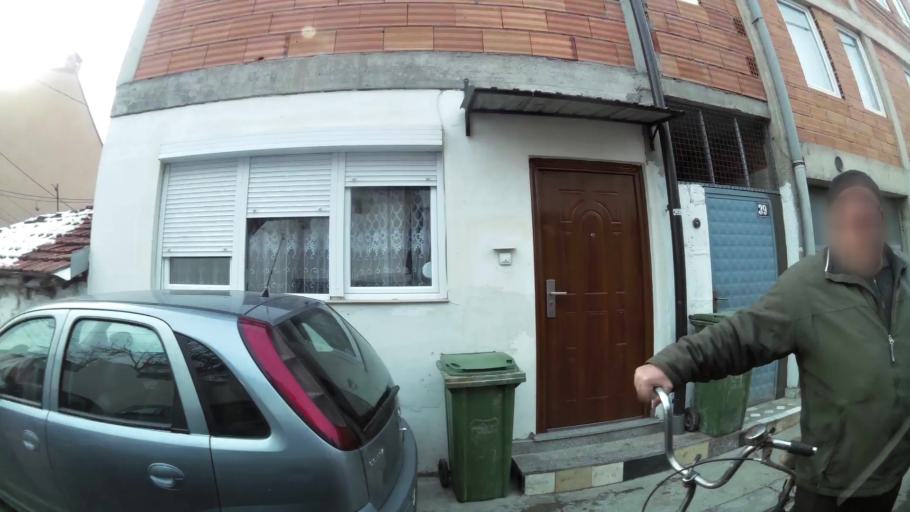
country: MK
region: Cair
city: Cair
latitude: 42.0025
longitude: 21.4464
